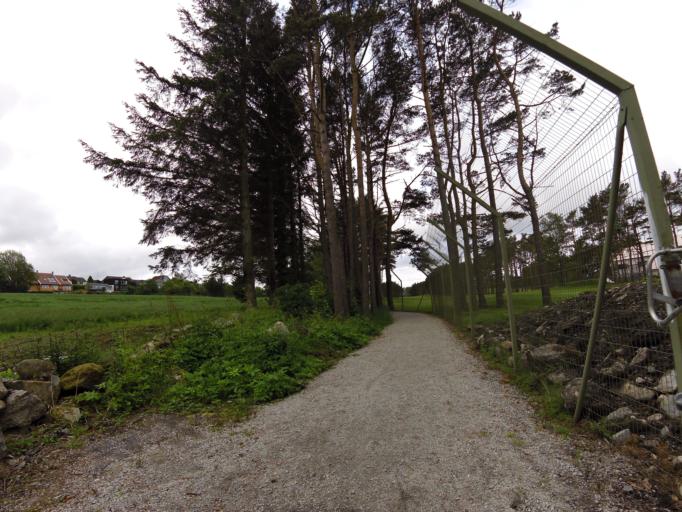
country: NO
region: Rogaland
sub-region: Randaberg
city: Randaberg
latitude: 58.9575
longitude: 5.6642
